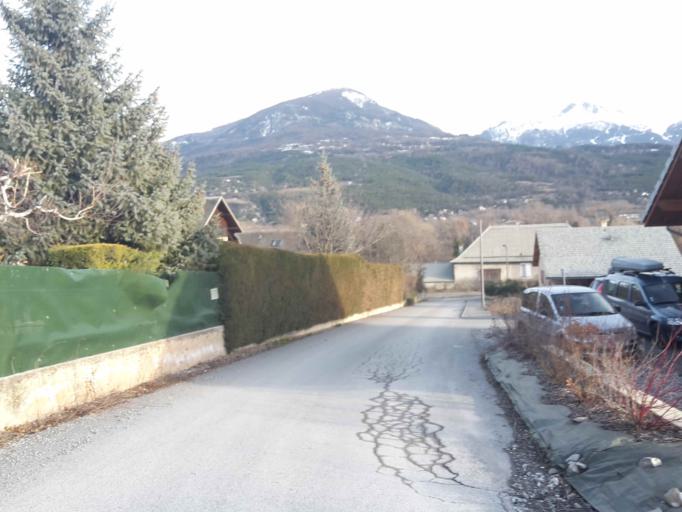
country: FR
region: Provence-Alpes-Cote d'Azur
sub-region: Departement des Hautes-Alpes
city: Embrun
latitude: 44.5552
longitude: 6.4855
